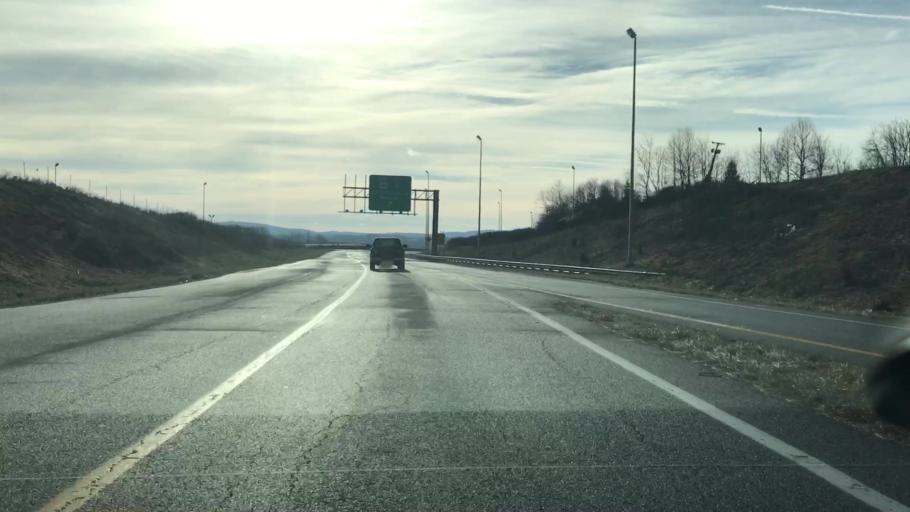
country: US
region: Virginia
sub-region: Montgomery County
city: Merrimac
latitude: 37.1911
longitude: -80.4026
